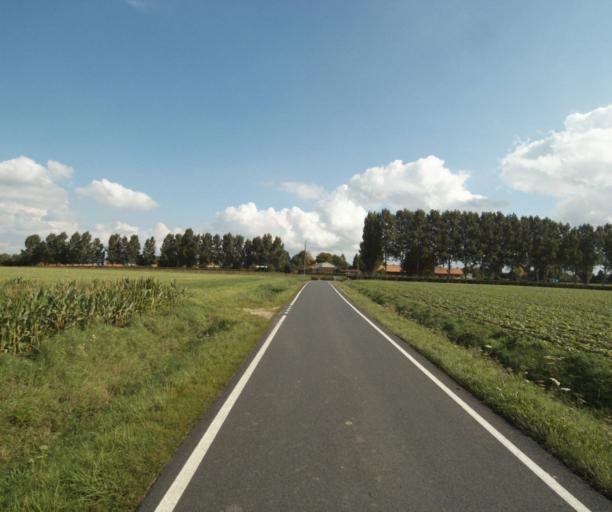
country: FR
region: Nord-Pas-de-Calais
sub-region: Departement du Nord
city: Herlies
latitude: 50.5782
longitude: 2.8446
